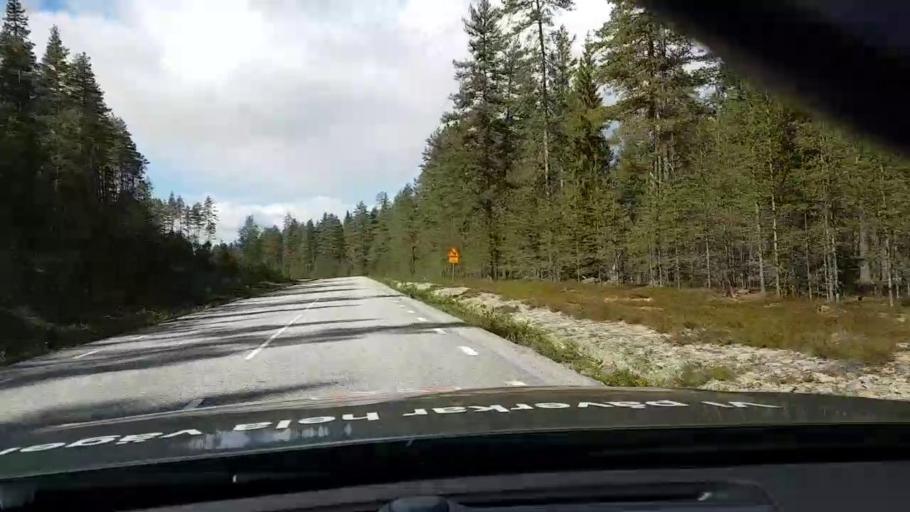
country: SE
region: Vaesternorrland
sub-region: OErnskoeldsviks Kommun
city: Bredbyn
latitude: 63.6741
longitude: 17.8185
